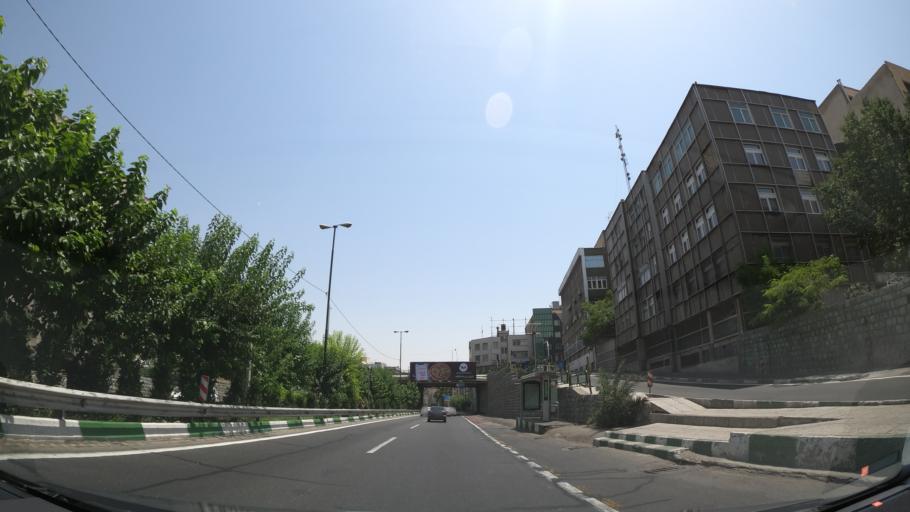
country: IR
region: Tehran
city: Tehran
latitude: 35.7249
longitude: 51.4246
